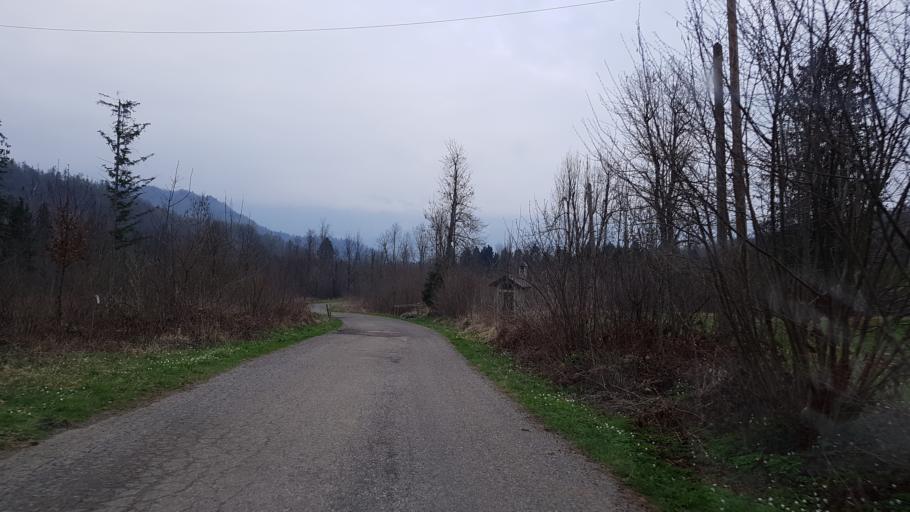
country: IT
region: Friuli Venezia Giulia
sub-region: Provincia di Udine
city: Faedis
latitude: 46.1973
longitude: 13.4005
